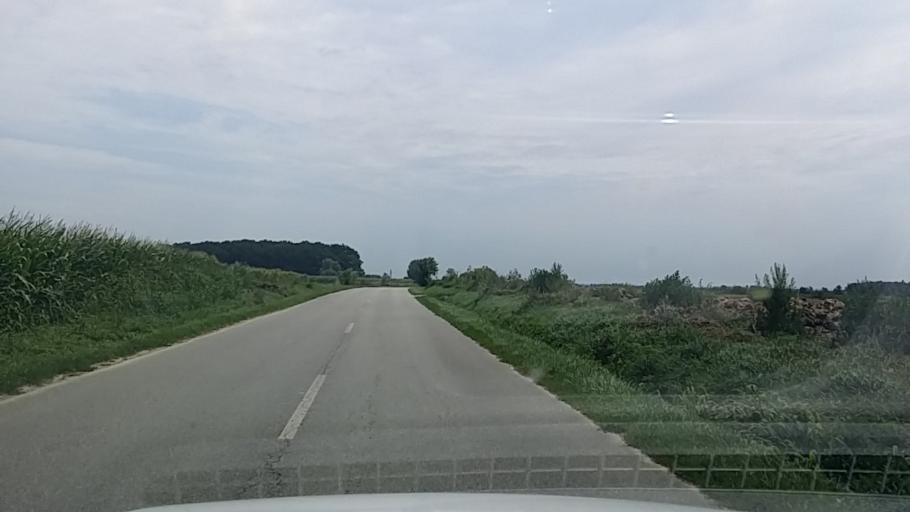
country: HU
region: Zala
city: Becsehely
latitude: 46.4171
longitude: 16.7704
